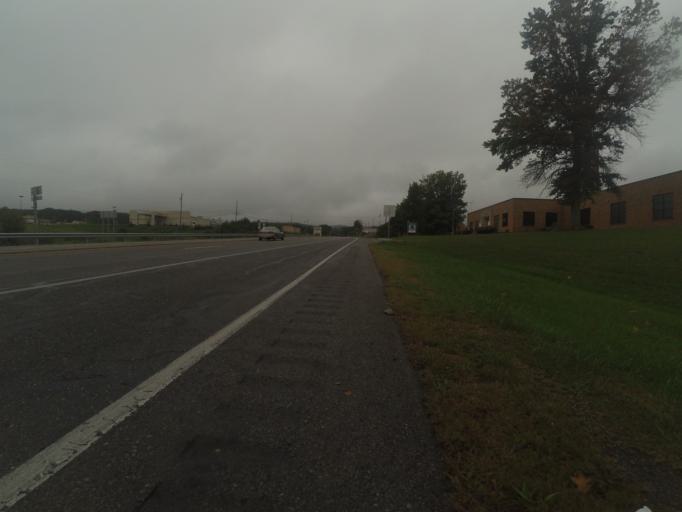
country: US
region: Pennsylvania
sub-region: Huntingdon County
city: Huntingdon
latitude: 40.4924
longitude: -78.0403
